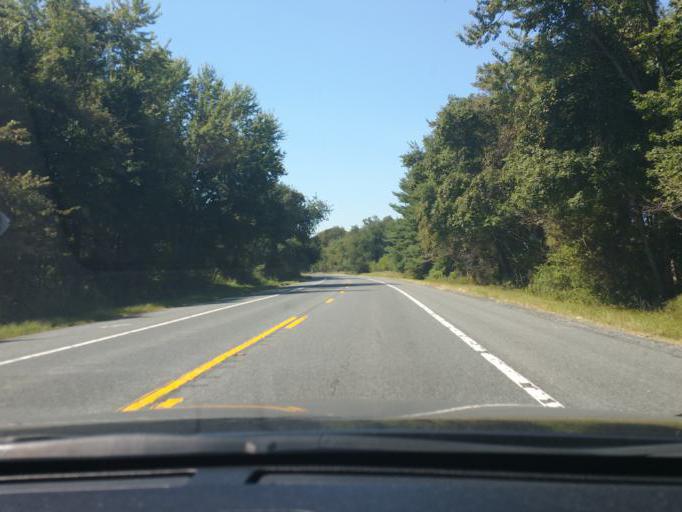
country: US
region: Maryland
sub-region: Harford County
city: Aberdeen
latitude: 39.5753
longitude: -76.1541
